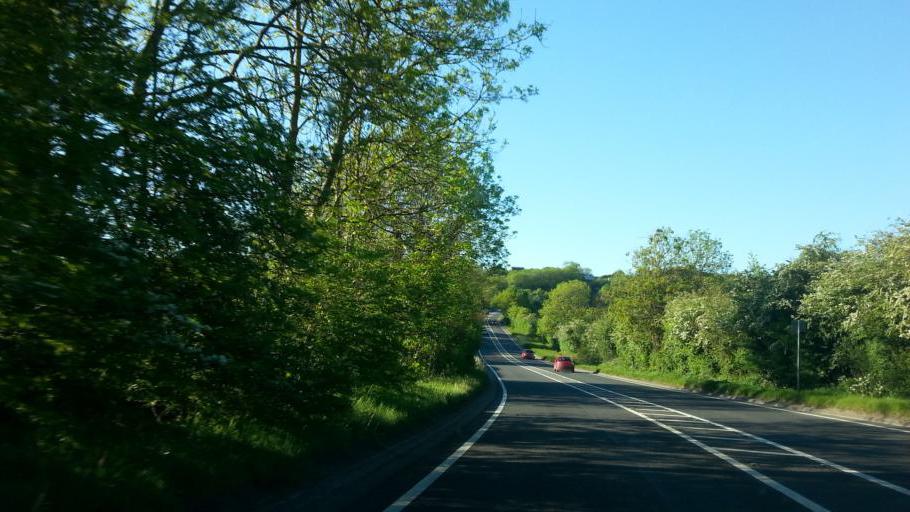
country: GB
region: England
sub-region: Bath and North East Somerset
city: Publow
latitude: 51.3868
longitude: -2.5506
